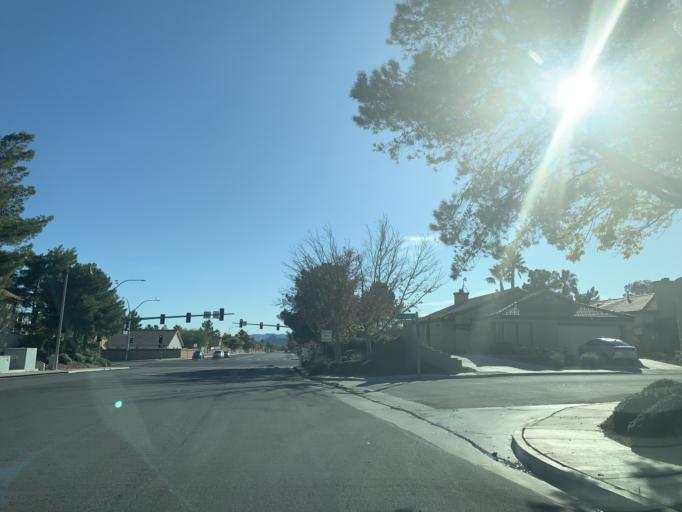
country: US
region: Nevada
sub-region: Clark County
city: Summerlin South
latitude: 36.1307
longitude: -115.3063
